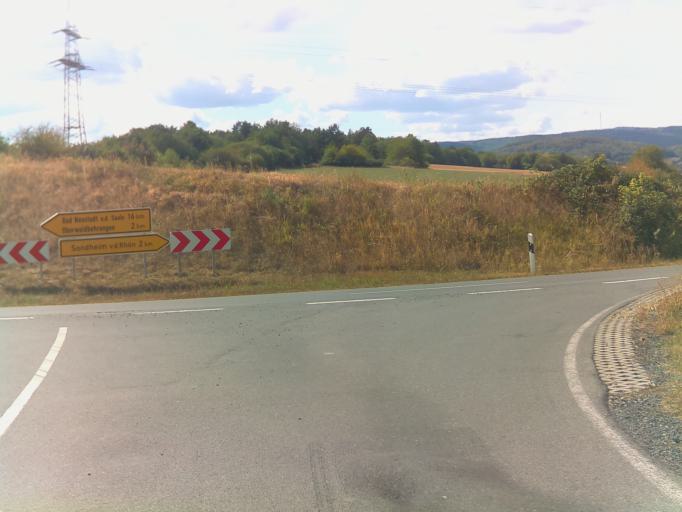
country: DE
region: Bavaria
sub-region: Regierungsbezirk Unterfranken
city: Sondheim vor der Rhoen
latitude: 50.4470
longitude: 10.1742
